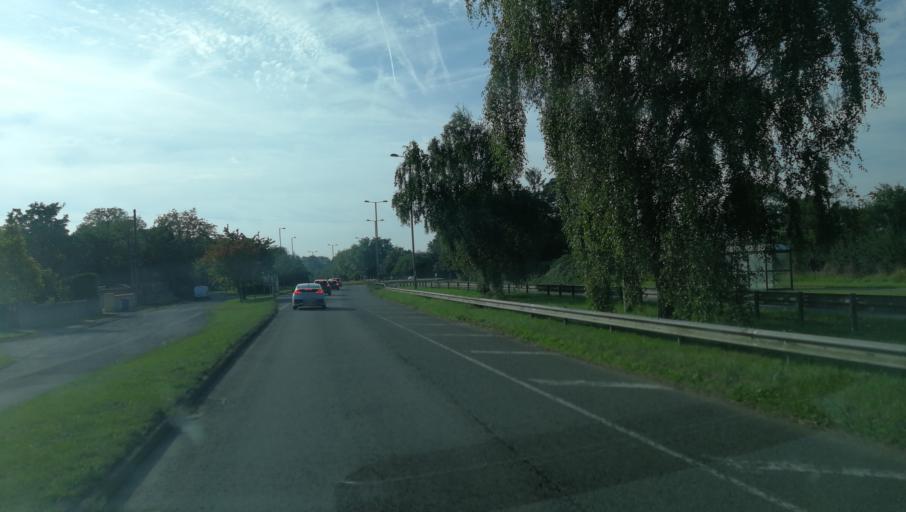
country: GB
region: England
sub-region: Oxfordshire
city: Yarnton
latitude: 51.8151
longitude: -1.3145
